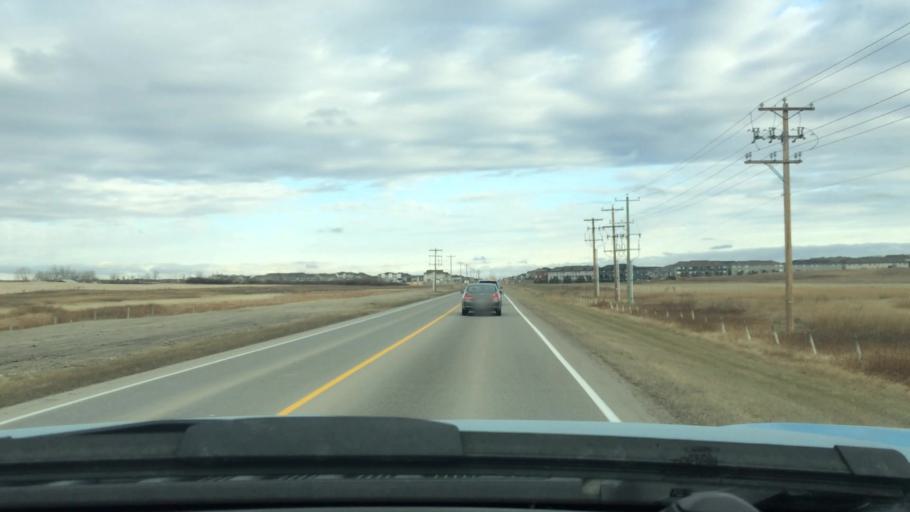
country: CA
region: Alberta
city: Airdrie
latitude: 51.2440
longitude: -114.0250
